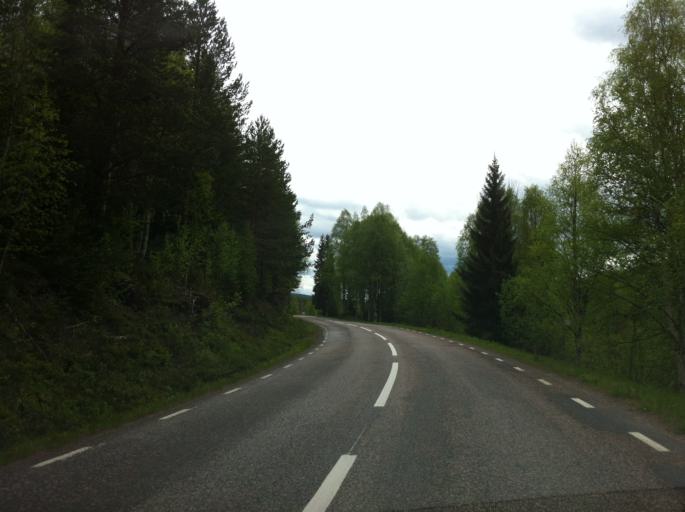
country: SE
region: Dalarna
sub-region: Malung-Saelens kommun
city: Malung
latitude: 61.2878
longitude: 13.1591
